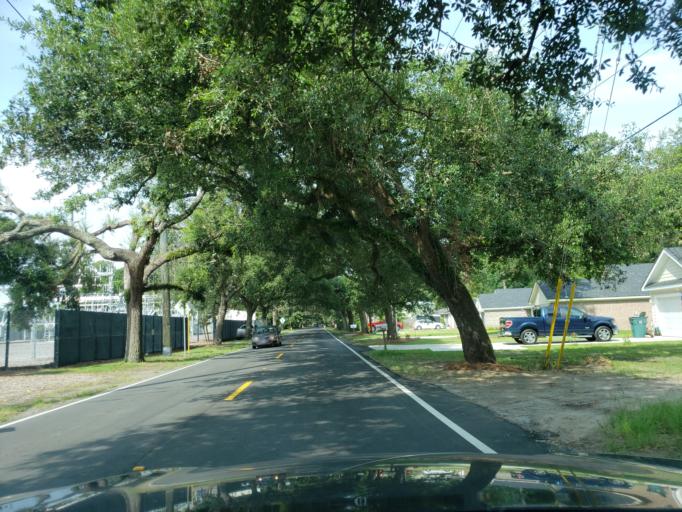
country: US
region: Georgia
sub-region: Chatham County
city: Wilmington Island
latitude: 32.0220
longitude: -80.9701
